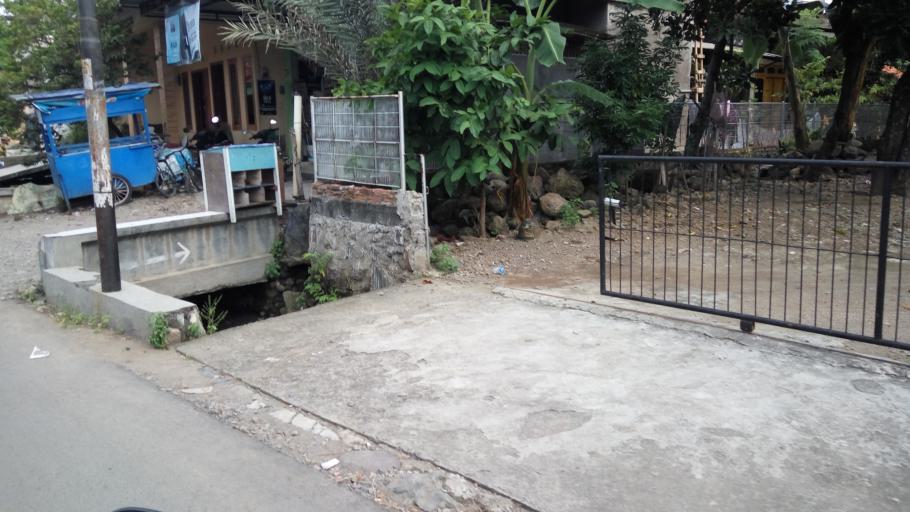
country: ID
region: Central Java
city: Mranggen
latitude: -7.0363
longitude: 110.4684
